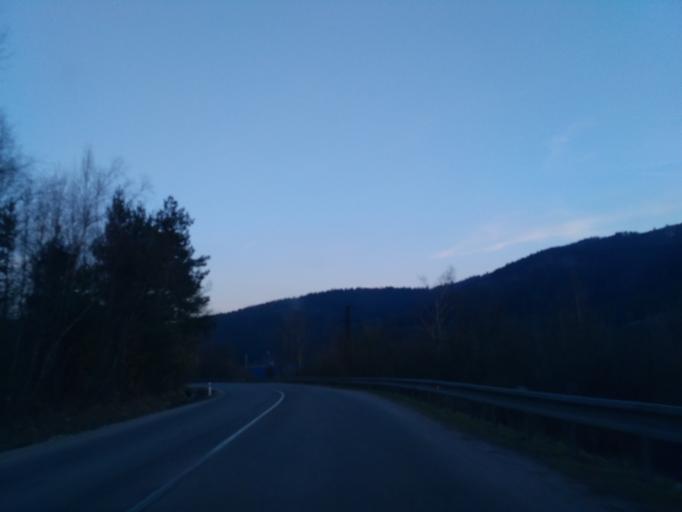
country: SK
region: Kosicky
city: Gelnica
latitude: 48.8223
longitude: 20.8855
